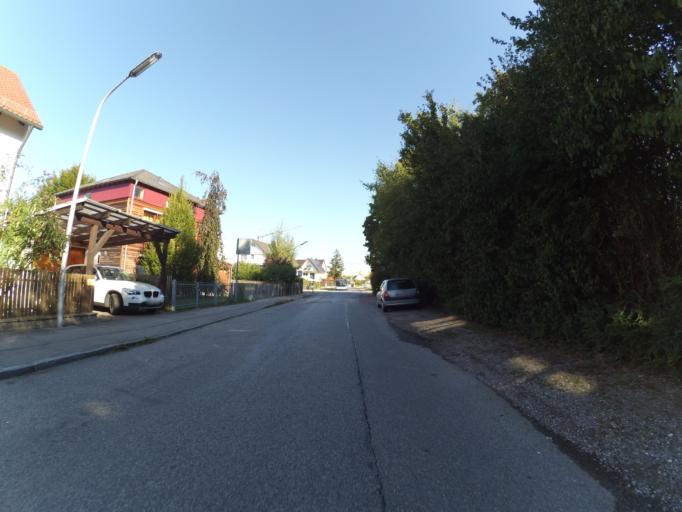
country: DE
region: Bavaria
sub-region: Upper Bavaria
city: Oberschleissheim
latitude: 48.1996
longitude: 11.5536
